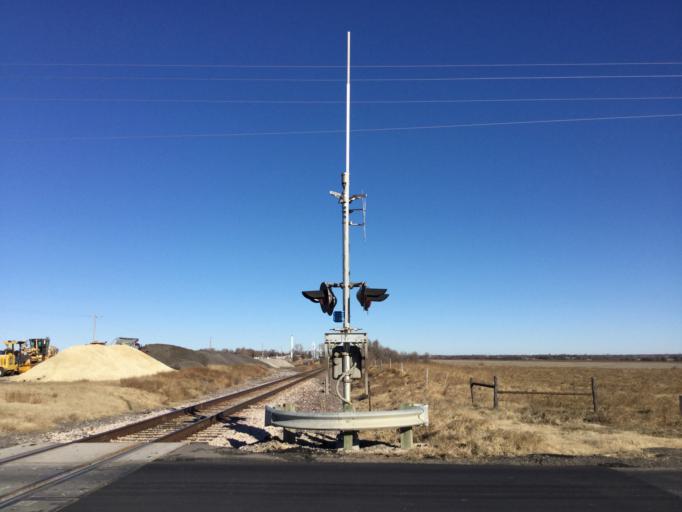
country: US
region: Kansas
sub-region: Marion County
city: Peabody
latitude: 38.0437
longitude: -97.1252
